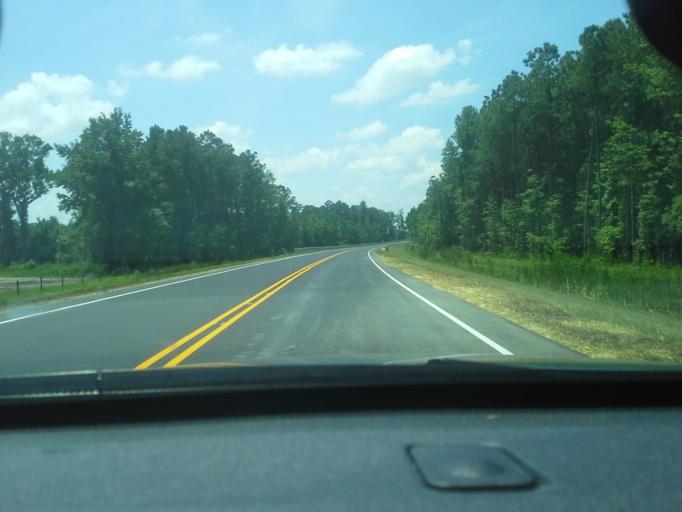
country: US
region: North Carolina
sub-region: Chowan County
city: Edenton
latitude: 35.9300
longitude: -76.5117
